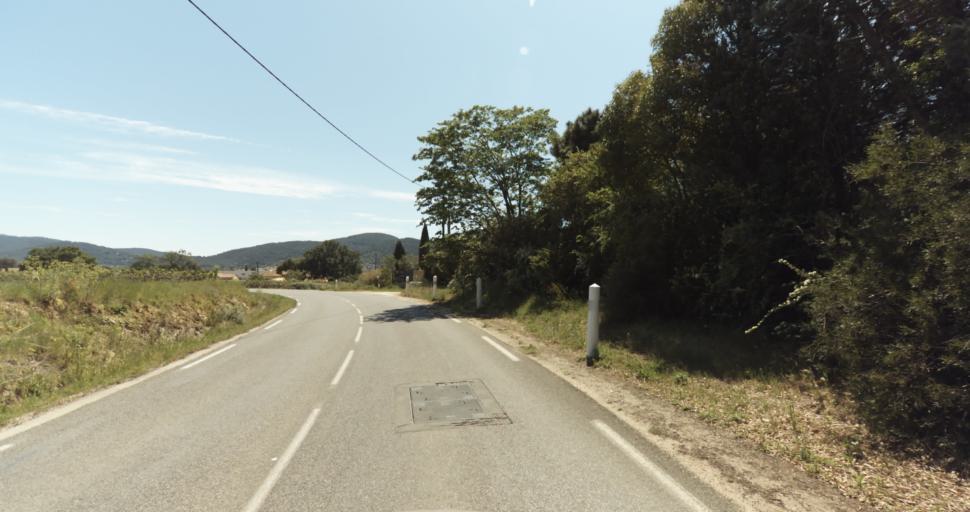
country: FR
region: Provence-Alpes-Cote d'Azur
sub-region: Departement du Var
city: La Crau
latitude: 43.1346
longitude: 6.0763
